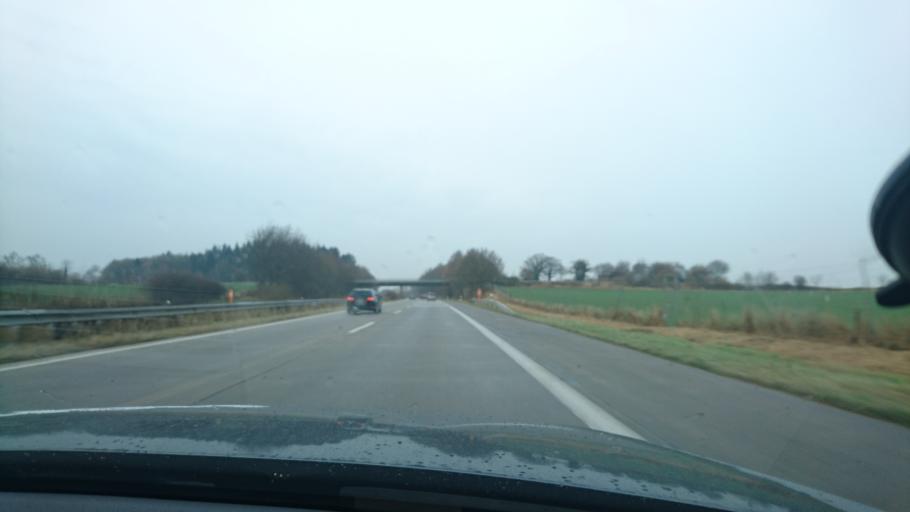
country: DE
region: Schleswig-Holstein
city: Ratekau
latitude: 53.9865
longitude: 10.7338
